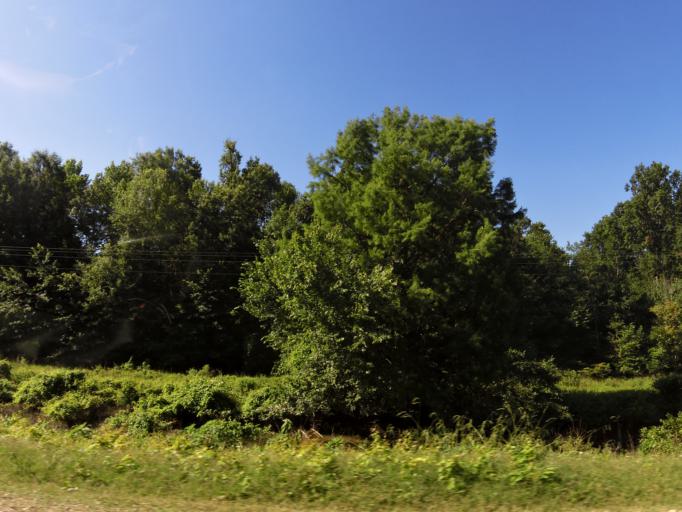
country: US
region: Arkansas
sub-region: Clay County
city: Corning
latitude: 36.4003
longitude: -90.5317
